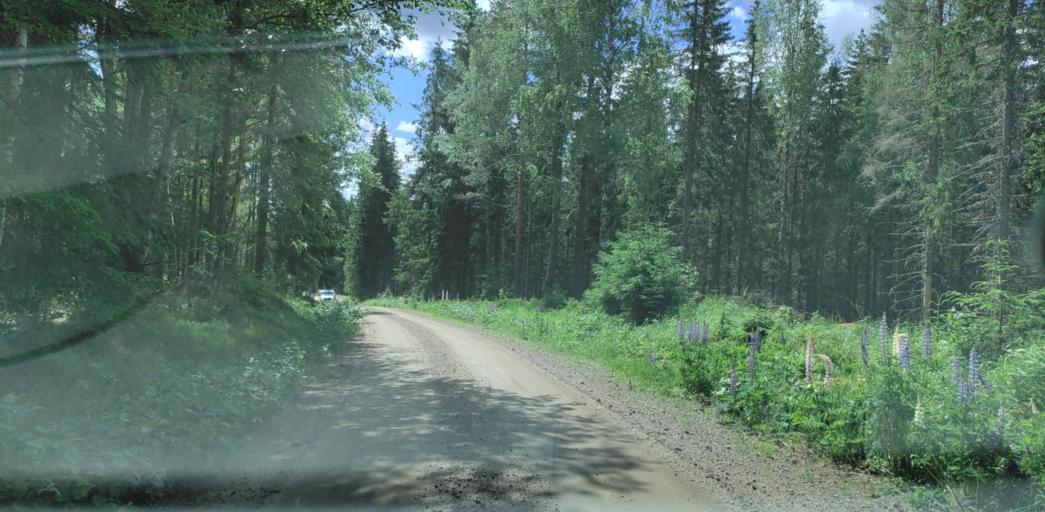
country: SE
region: Vaermland
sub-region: Hagfors Kommun
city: Ekshaerad
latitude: 60.0676
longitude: 13.3077
